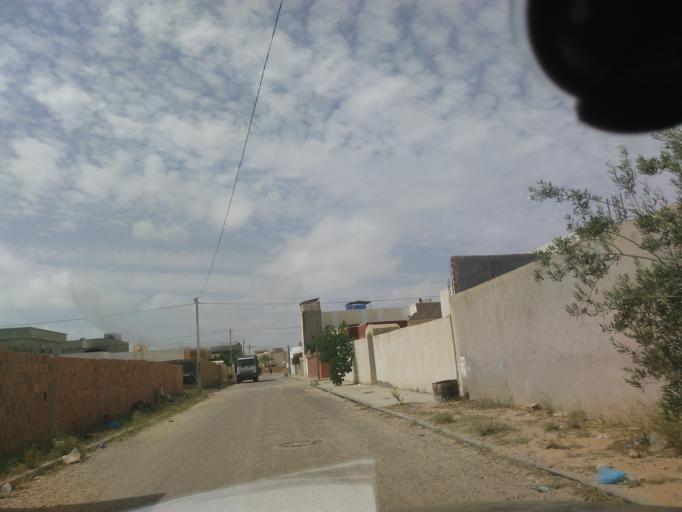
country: TN
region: Tataouine
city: Tataouine
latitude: 32.9524
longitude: 10.4655
